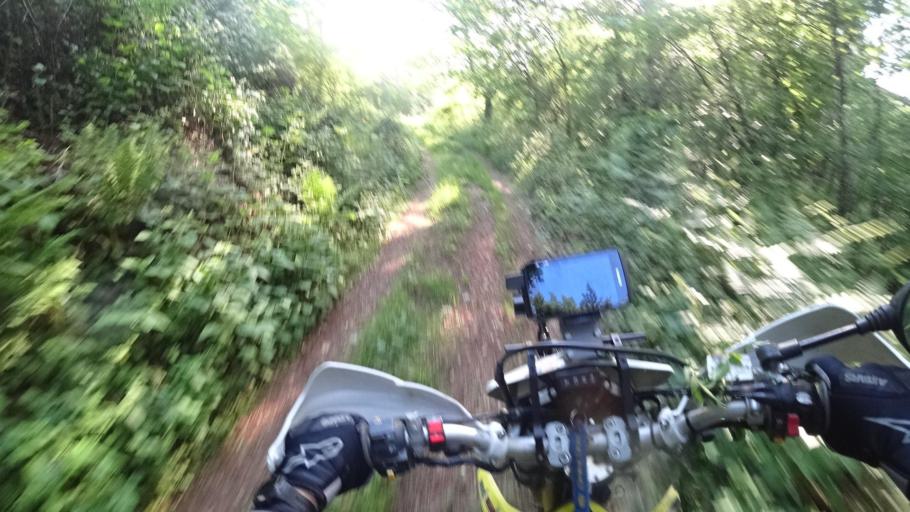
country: BA
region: Federation of Bosnia and Herzegovina
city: Sanica
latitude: 44.6331
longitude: 16.6771
